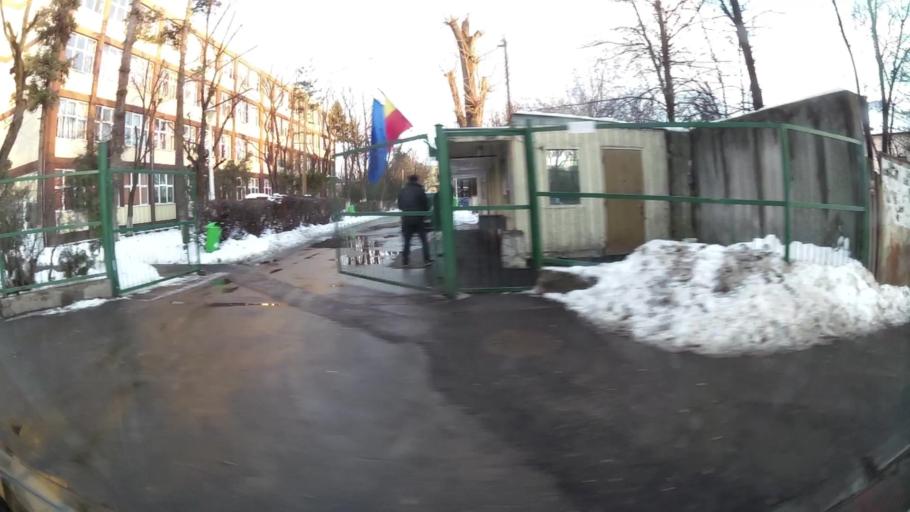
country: RO
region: Ilfov
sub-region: Comuna Popesti-Leordeni
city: Popesti-Leordeni
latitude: 44.3803
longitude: 26.1423
